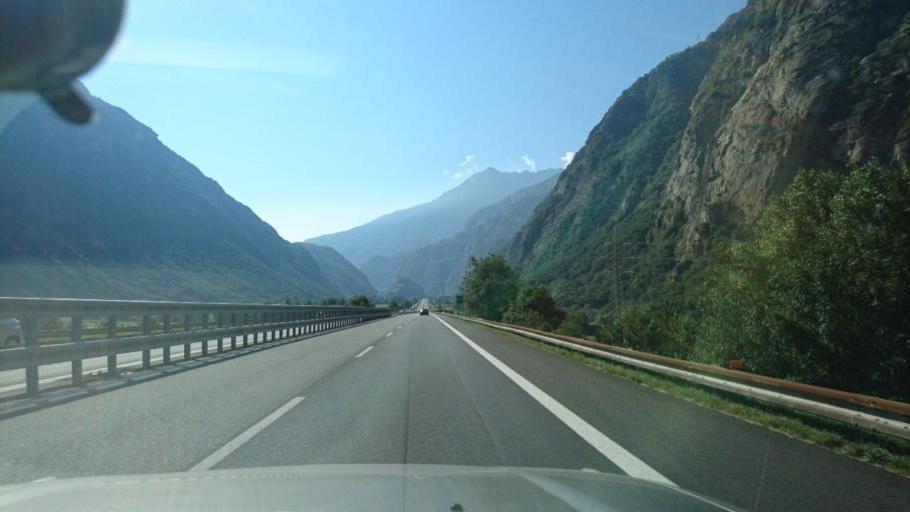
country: IT
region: Aosta Valley
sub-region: Valle d'Aosta
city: Arnad
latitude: 45.6350
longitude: 7.7248
